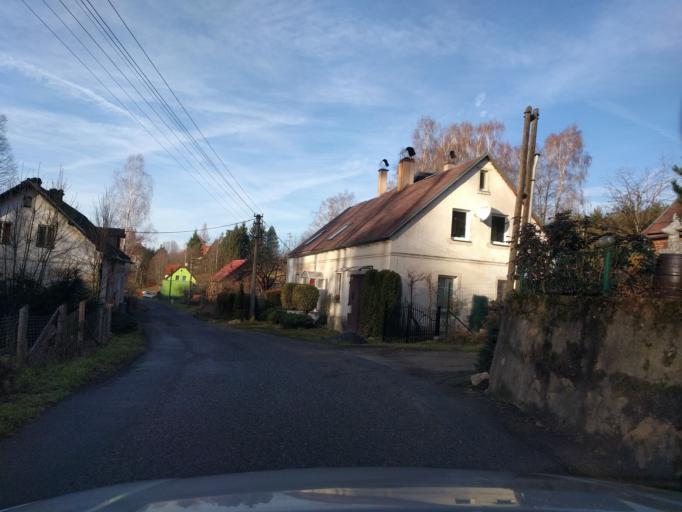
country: PL
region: Silesian Voivodeship
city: Zawidow
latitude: 50.9821
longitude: 15.0832
